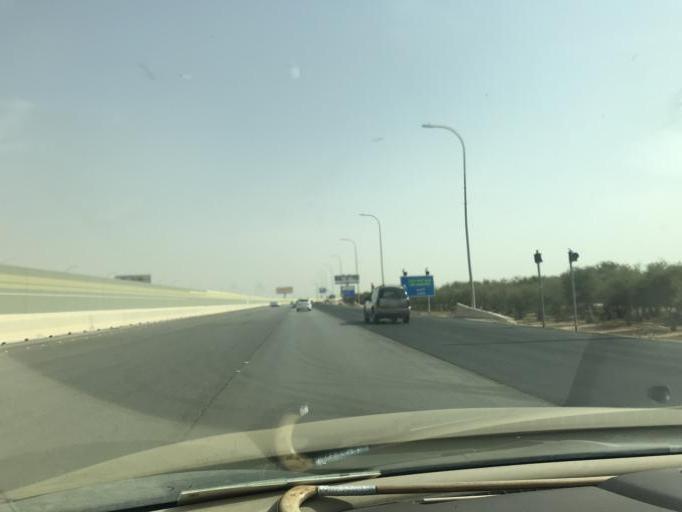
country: SA
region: Ar Riyad
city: Riyadh
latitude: 24.9228
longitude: 46.7205
